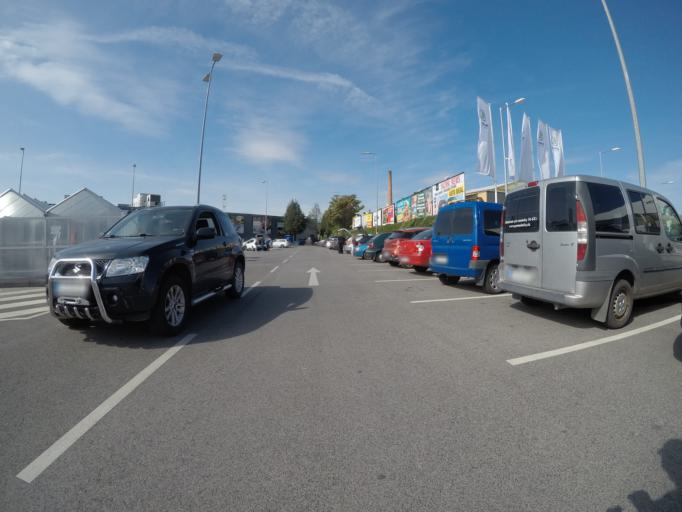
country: SK
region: Trnavsky
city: Dunajska Streda
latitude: 47.9966
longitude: 17.6267
